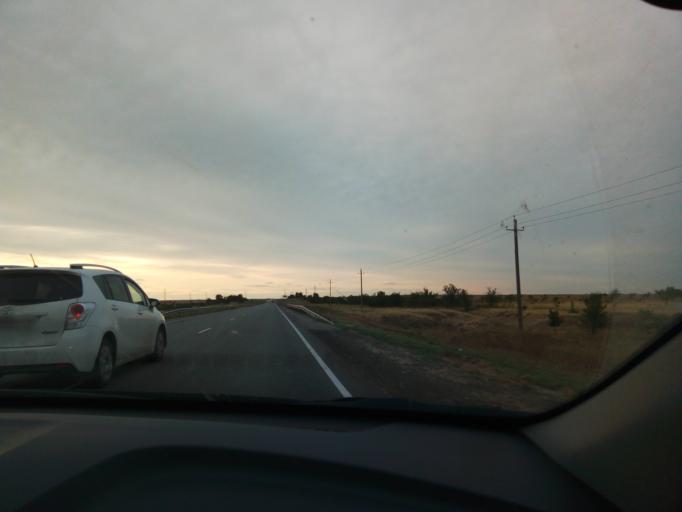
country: RU
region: Volgograd
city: Primorsk
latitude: 49.2464
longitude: 44.8914
